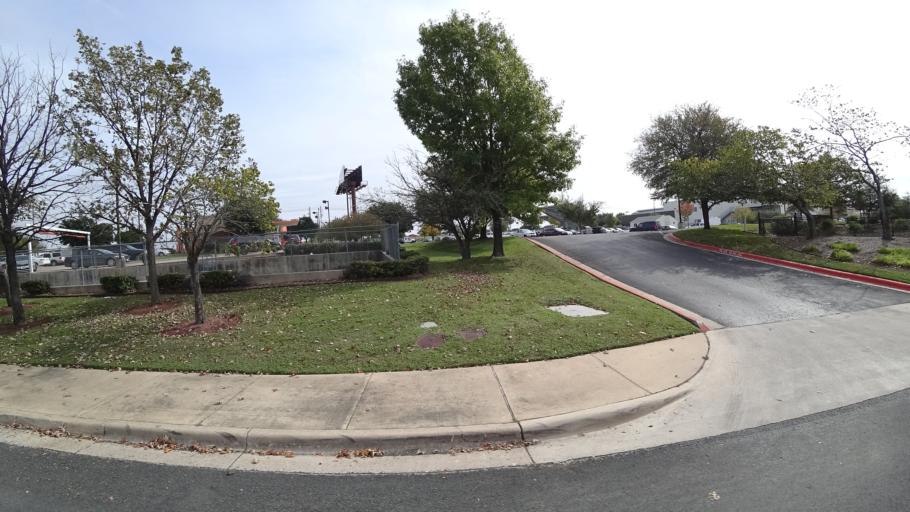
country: US
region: Texas
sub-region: Travis County
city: Wells Branch
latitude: 30.4332
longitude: -97.6716
